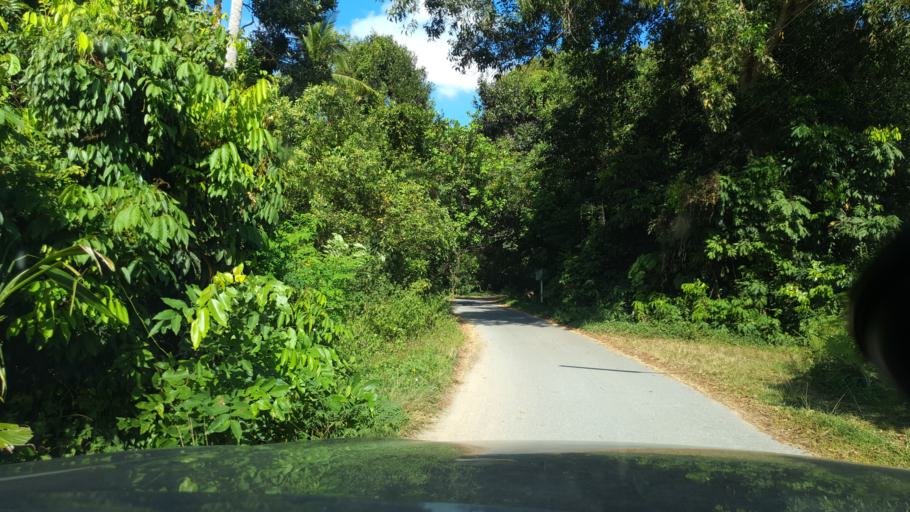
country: TH
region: Krabi
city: Krabi
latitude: 8.0227
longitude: 98.8794
